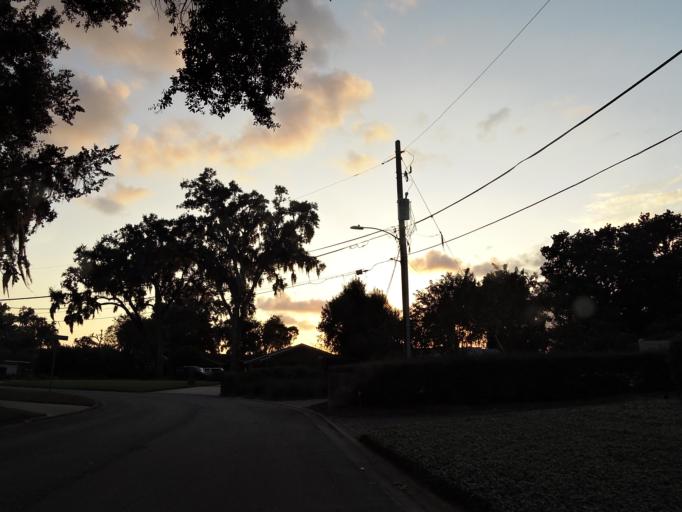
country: US
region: Florida
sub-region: Clay County
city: Orange Park
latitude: 30.1911
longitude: -81.6327
